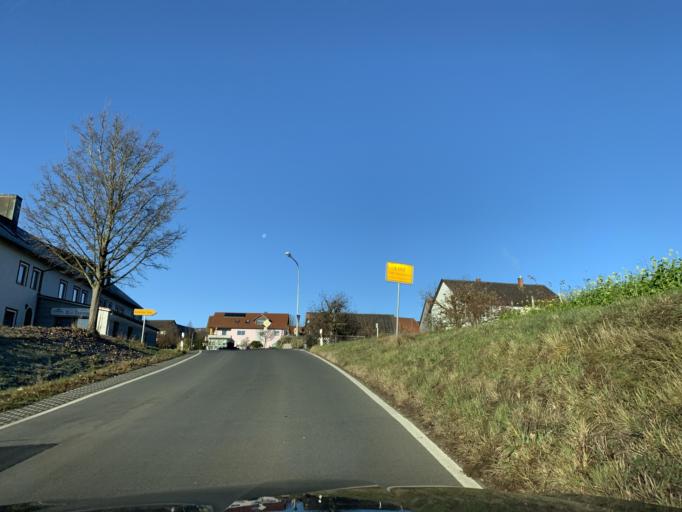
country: DE
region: Bavaria
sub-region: Upper Palatinate
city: Winklarn
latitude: 49.4640
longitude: 12.4693
